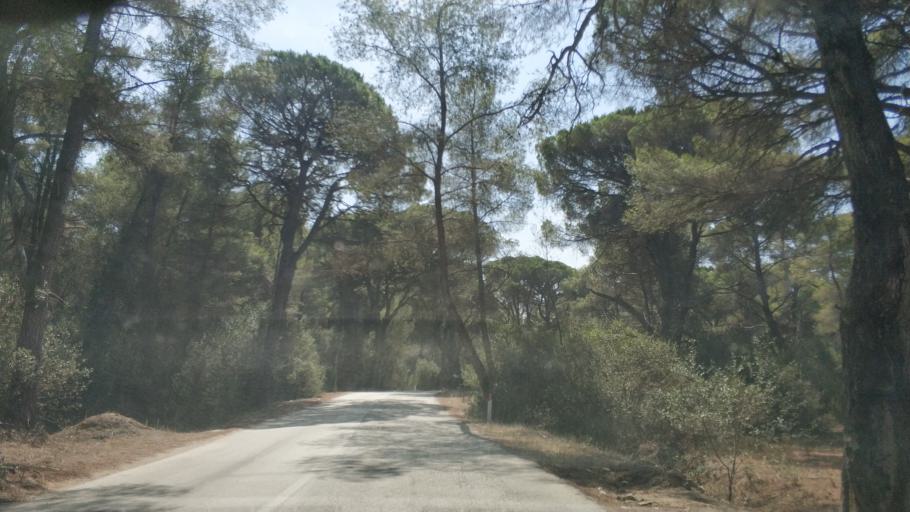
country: AL
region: Fier
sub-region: Rrethi i Lushnjes
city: Divjake
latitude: 40.9857
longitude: 19.4833
